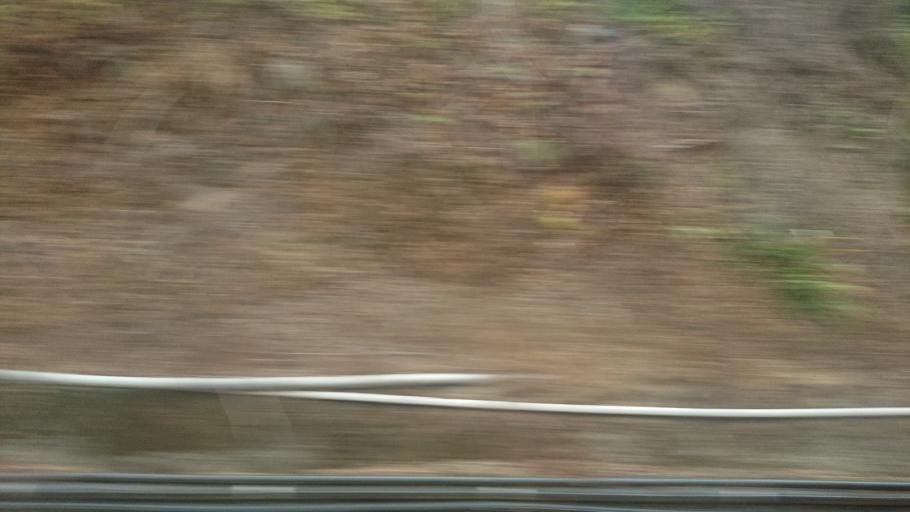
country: TW
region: Taiwan
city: Lugu
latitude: 23.6093
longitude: 120.7126
